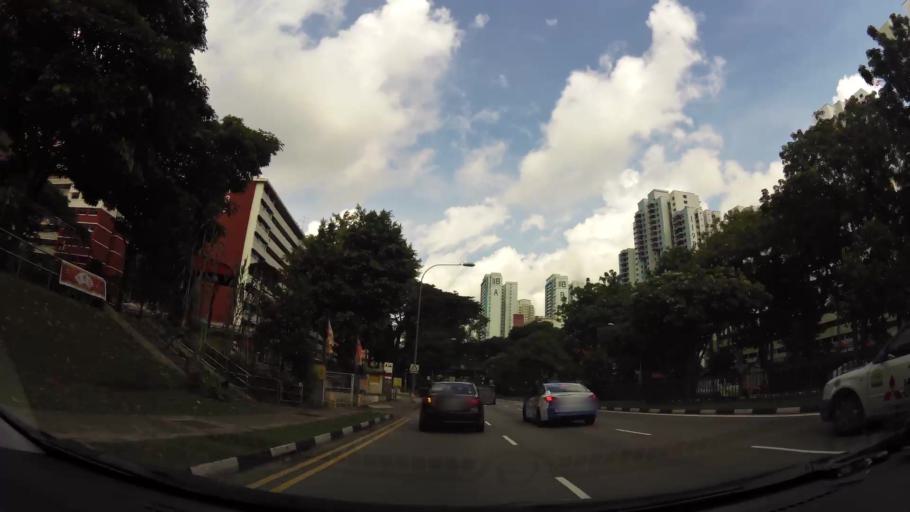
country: SG
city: Singapore
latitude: 1.2794
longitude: 103.8284
